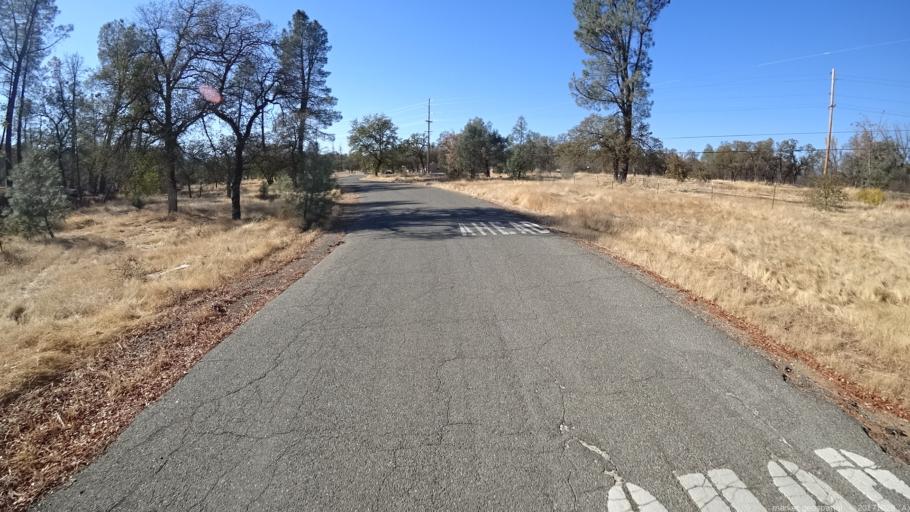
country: US
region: California
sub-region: Shasta County
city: Central Valley (historical)
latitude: 40.6373
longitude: -122.3775
